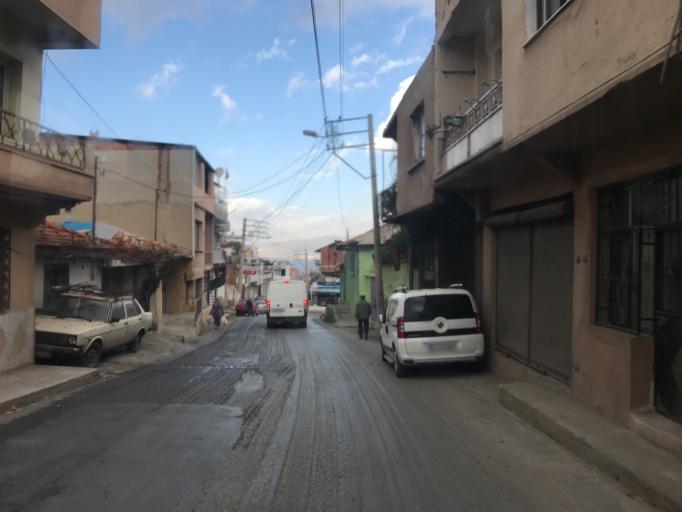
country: TR
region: Izmir
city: Buca
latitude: 38.4082
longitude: 27.1623
